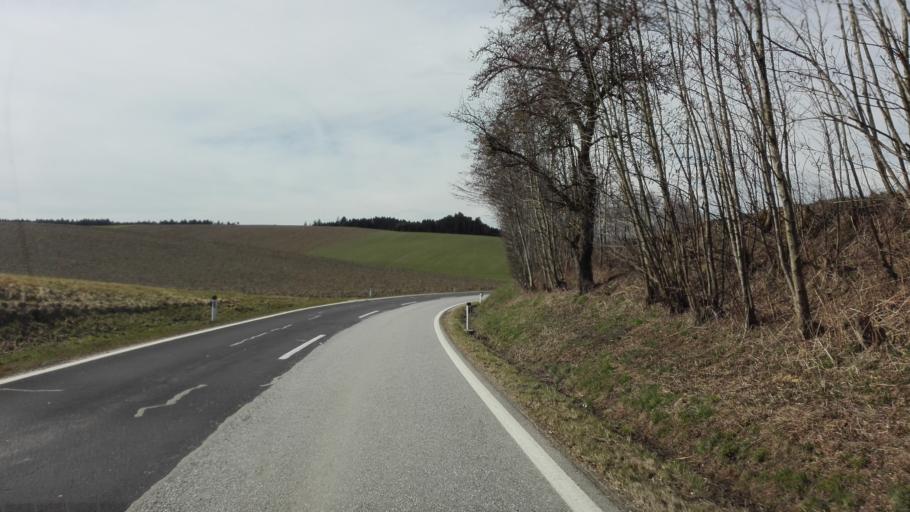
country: DE
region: Bavaria
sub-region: Lower Bavaria
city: Obernzell
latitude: 48.3724
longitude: 13.6353
